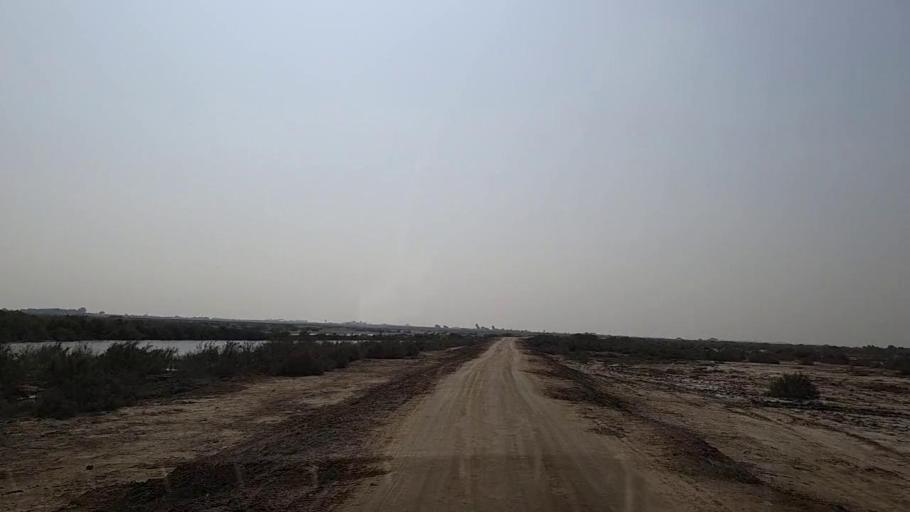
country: PK
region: Sindh
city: Gharo
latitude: 24.6775
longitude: 67.7331
